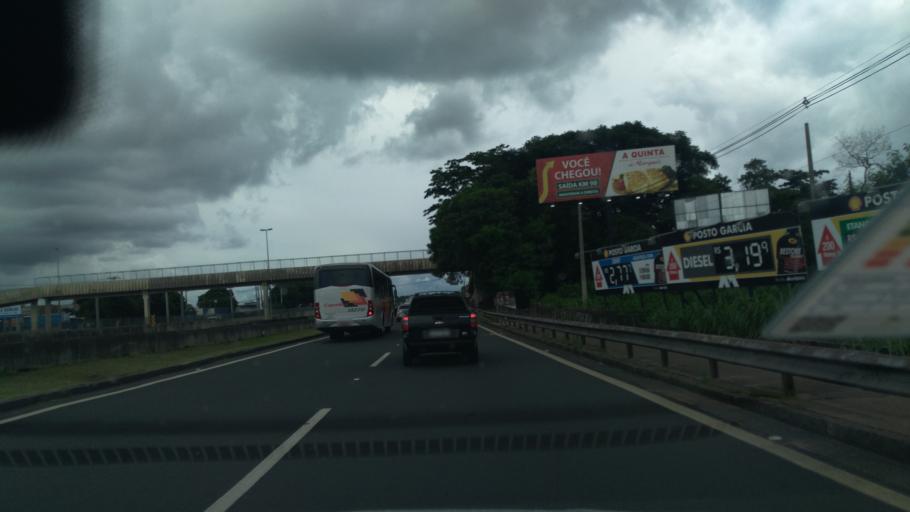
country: BR
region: Sao Paulo
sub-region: Campinas
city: Campinas
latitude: -22.8933
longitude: -47.1113
